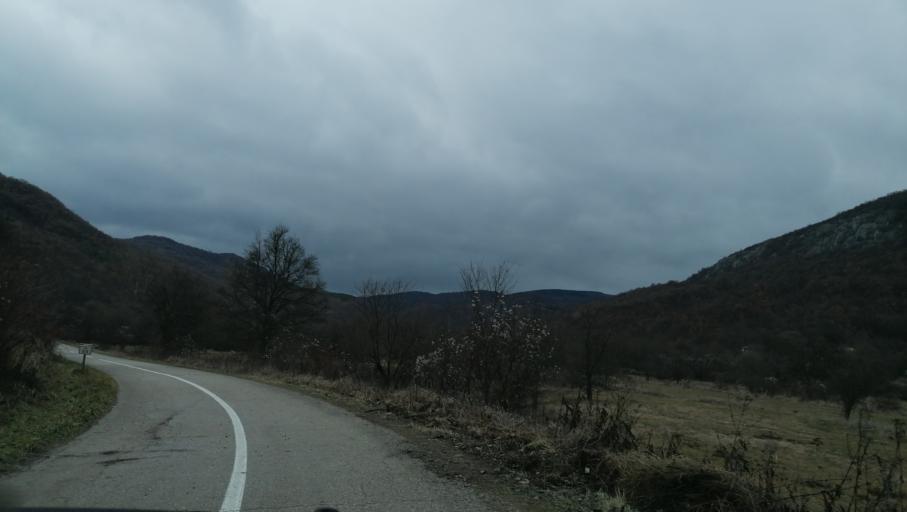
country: RS
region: Central Serbia
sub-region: Pirotski Okrug
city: Dimitrovgrad
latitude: 42.9331
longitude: 22.7753
